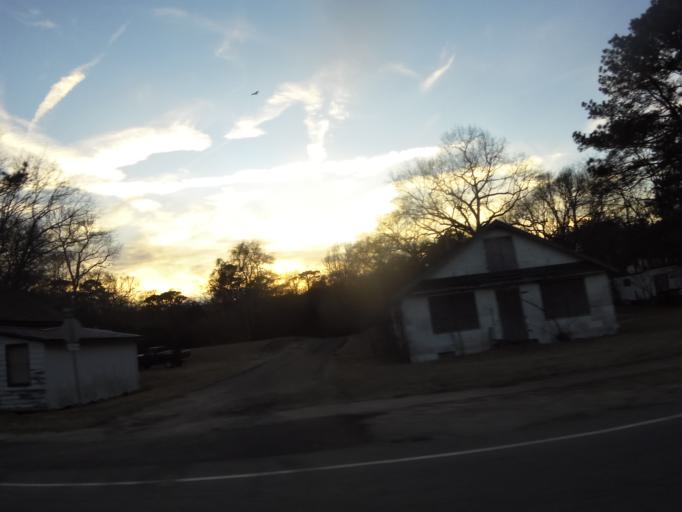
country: US
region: Virginia
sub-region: Southampton County
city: Courtland
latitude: 36.7222
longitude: -77.0703
